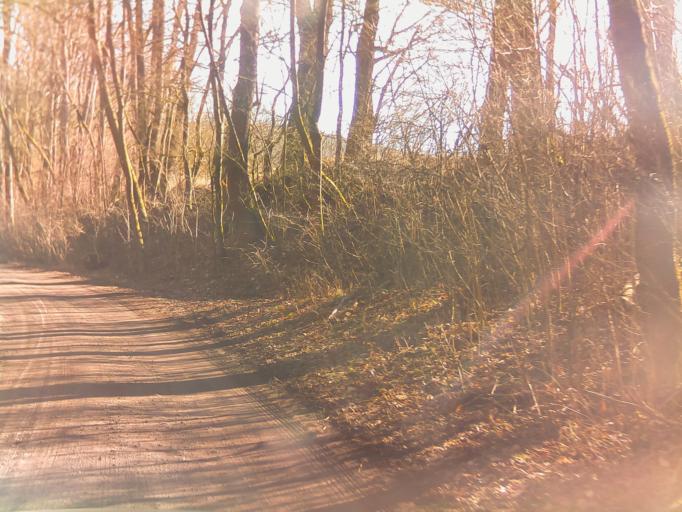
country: DE
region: Thuringia
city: Belrieth
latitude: 50.5398
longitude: 10.4995
